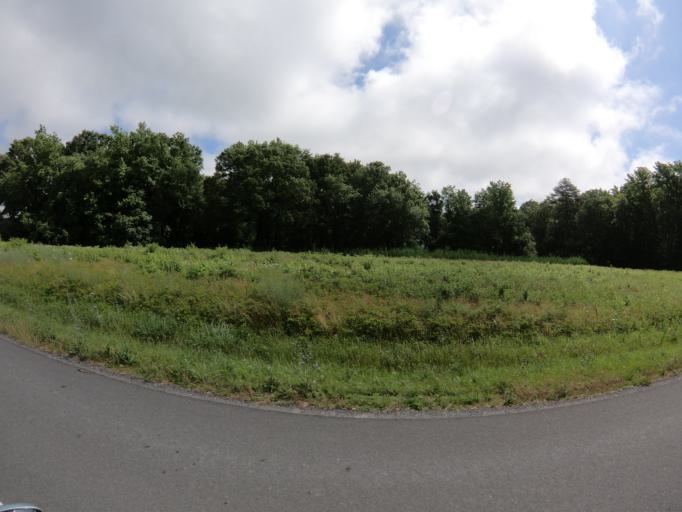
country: US
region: Maryland
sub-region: Caroline County
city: Greensboro
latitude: 39.0537
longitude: -75.8376
